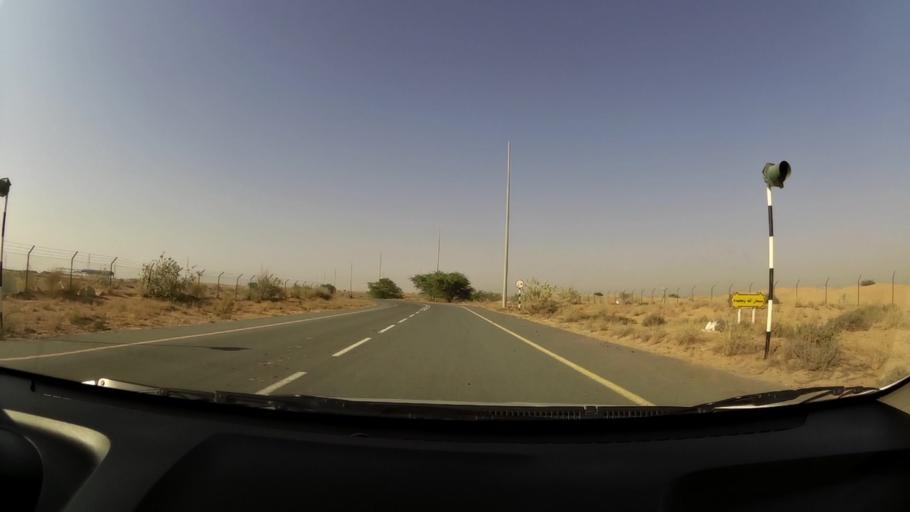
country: AE
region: Umm al Qaywayn
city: Umm al Qaywayn
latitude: 25.4341
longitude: 55.5936
